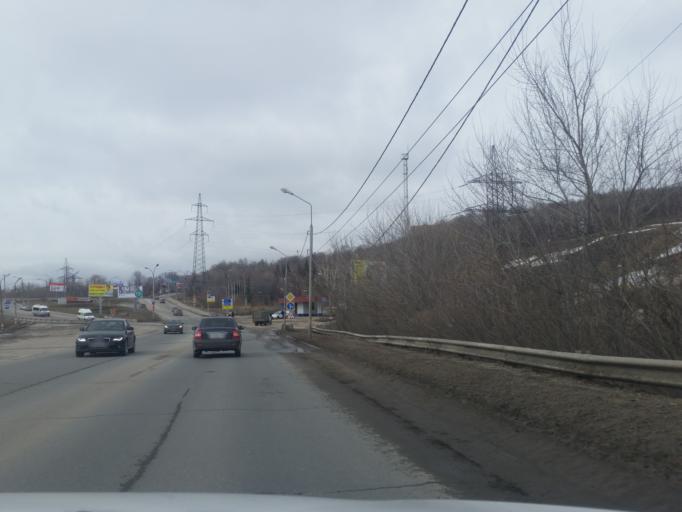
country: RU
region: Ulyanovsk
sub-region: Ulyanovskiy Rayon
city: Ulyanovsk
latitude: 54.3115
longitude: 48.4136
